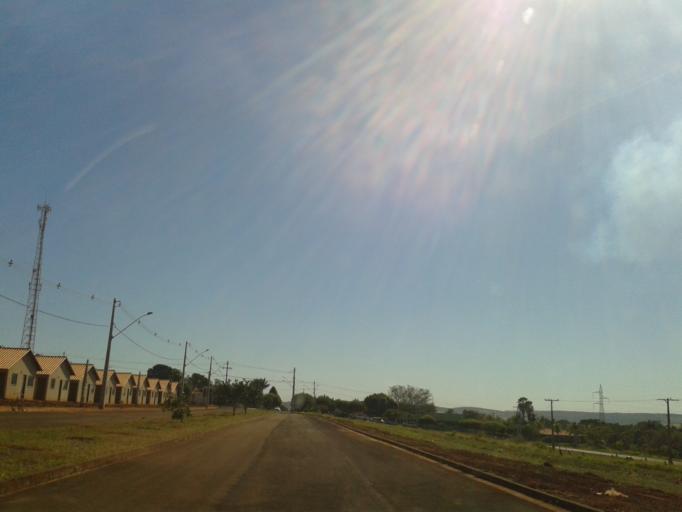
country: BR
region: Minas Gerais
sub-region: Capinopolis
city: Capinopolis
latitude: -18.5224
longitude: -49.5012
